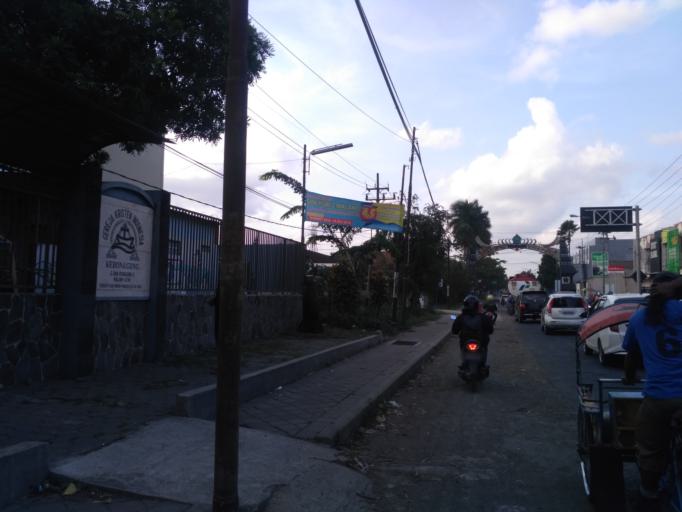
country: ID
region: East Java
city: Kebonsari
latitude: -8.0238
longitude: 112.6174
